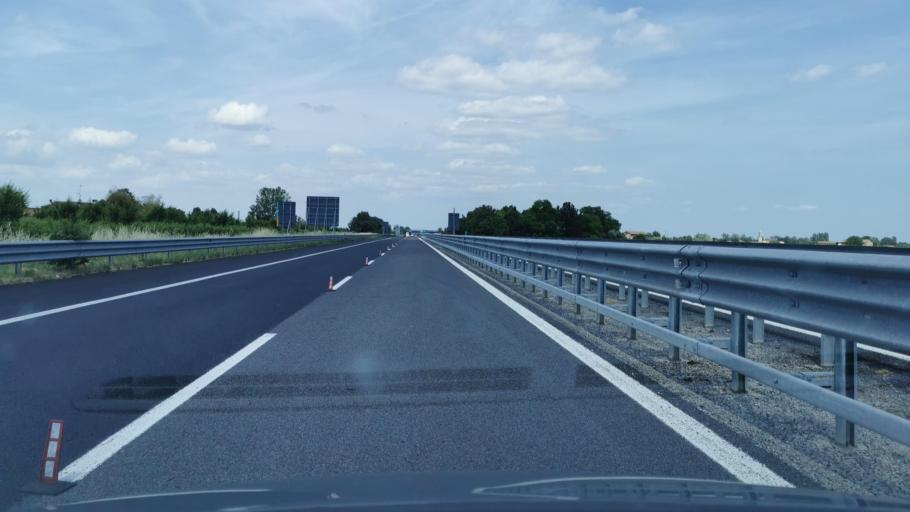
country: IT
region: Emilia-Romagna
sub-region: Provincia di Ravenna
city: Solarolo
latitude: 44.3592
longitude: 11.8218
